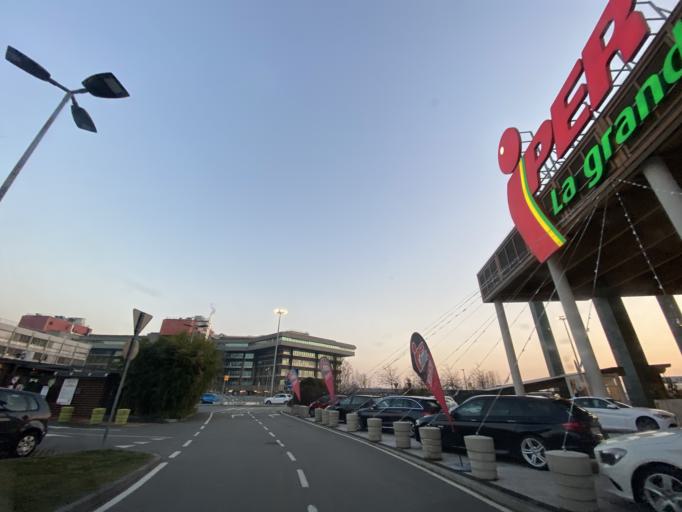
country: IT
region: Lombardy
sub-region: Citta metropolitana di Milano
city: Arese
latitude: 45.5639
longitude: 9.0567
